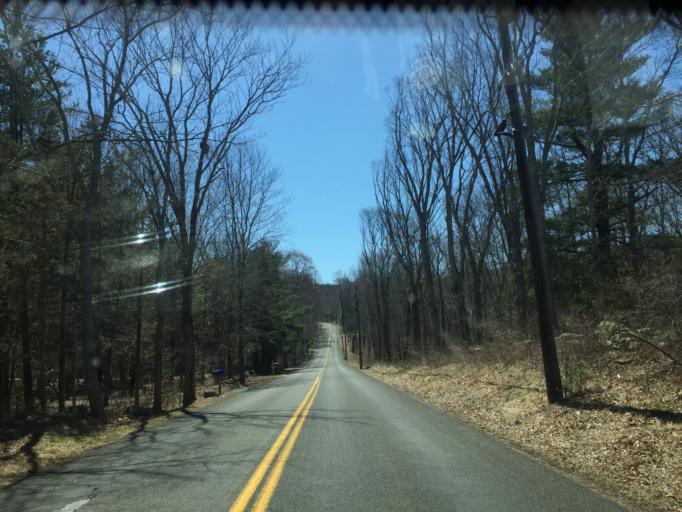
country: US
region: Connecticut
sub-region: Hartford County
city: Terramuggus
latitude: 41.6681
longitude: -72.4664
